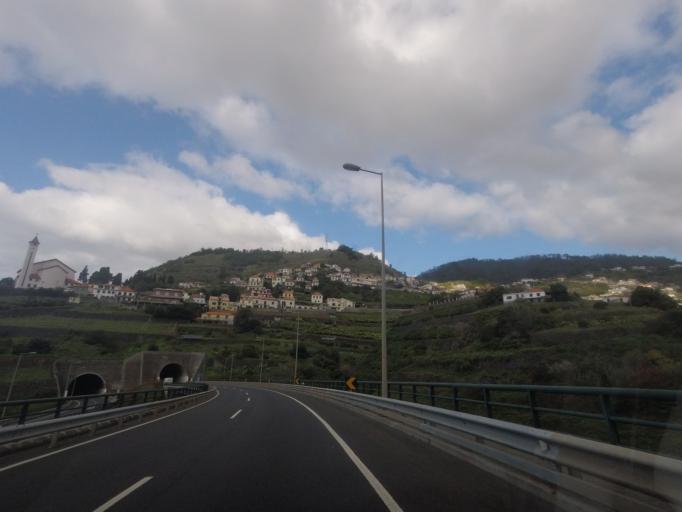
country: PT
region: Madeira
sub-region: Ribeira Brava
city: Campanario
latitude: 32.6682
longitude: -17.0279
